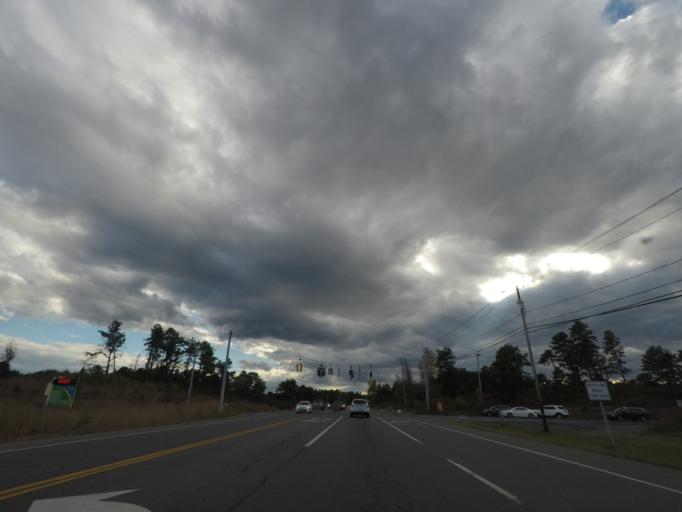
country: US
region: New York
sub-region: Albany County
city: Westmere
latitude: 42.7195
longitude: -73.8656
